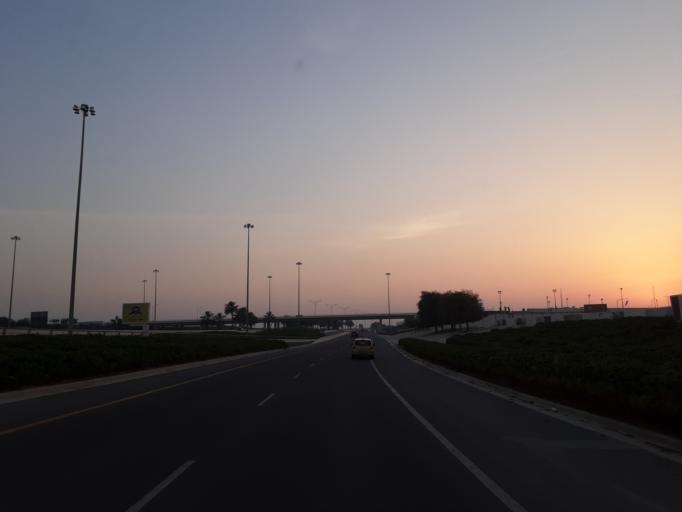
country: AE
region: Abu Dhabi
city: Abu Dhabi
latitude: 24.5306
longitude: 54.4283
